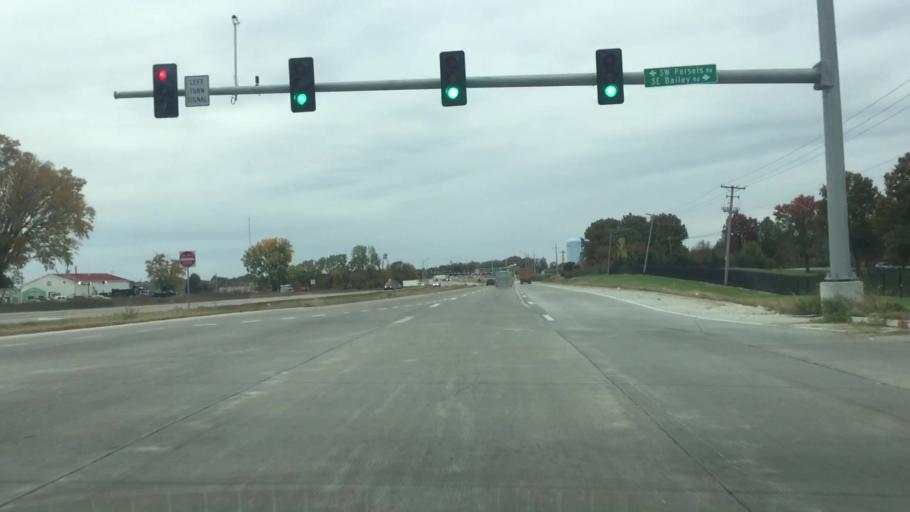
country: US
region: Missouri
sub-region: Jackson County
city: Lees Summit
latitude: 38.8962
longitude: -94.3753
